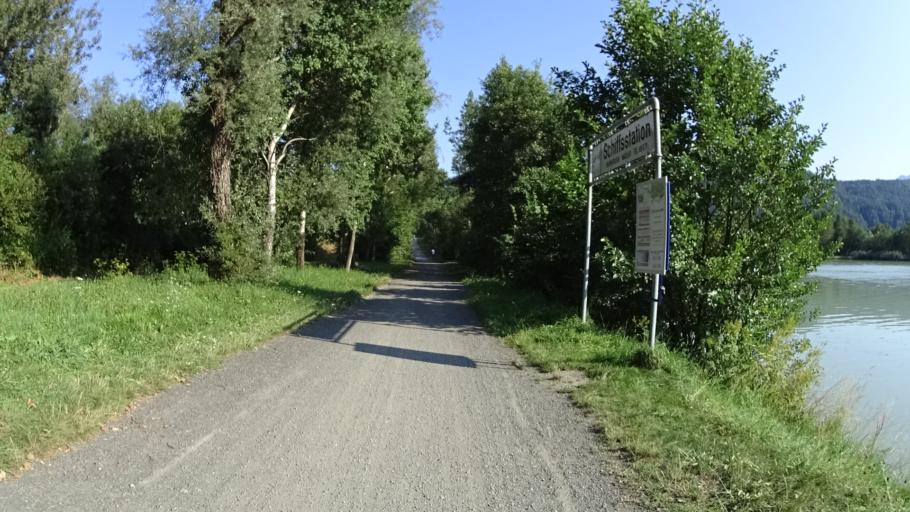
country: AT
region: Carinthia
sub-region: Politischer Bezirk Villach Land
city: Wernberg
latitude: 46.6005
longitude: 13.9488
